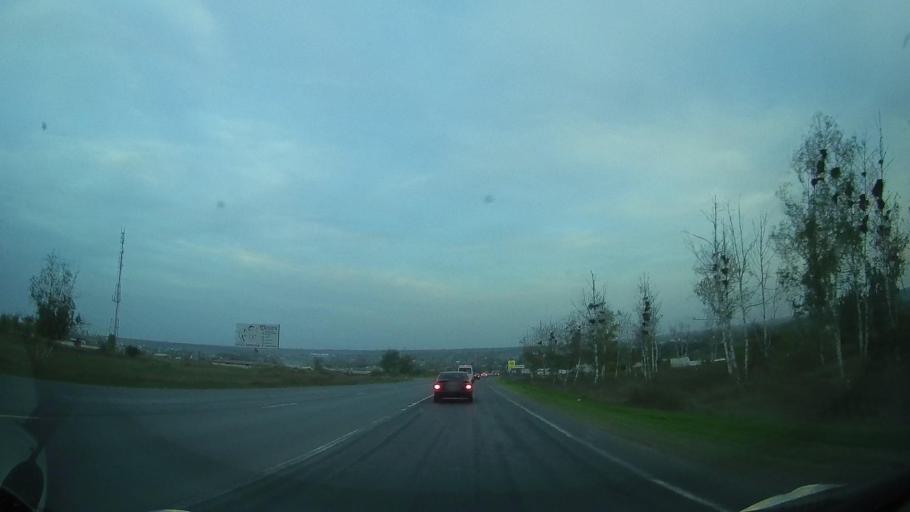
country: RU
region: Rostov
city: Kagal'nitskaya
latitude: 46.8885
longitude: 40.1387
